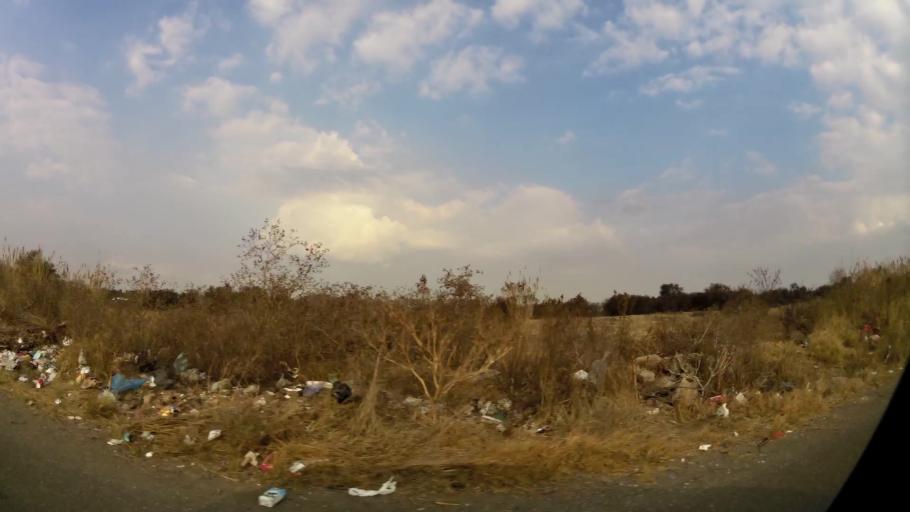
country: ZA
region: Gauteng
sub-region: Sedibeng District Municipality
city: Vereeniging
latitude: -26.6885
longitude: 27.9010
